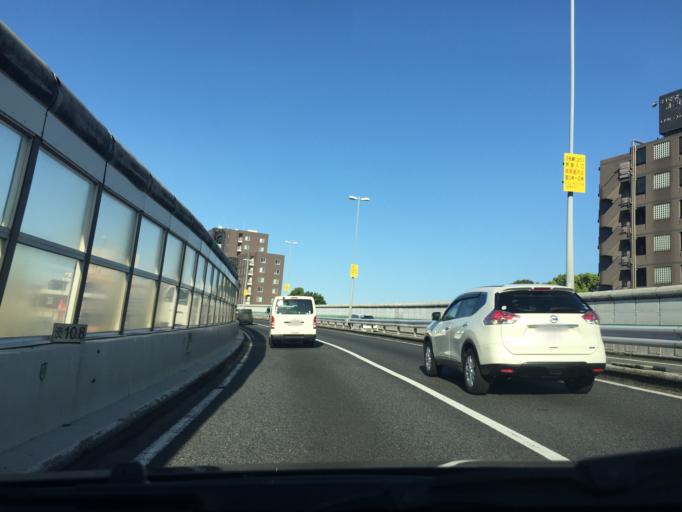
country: JP
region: Tokyo
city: Tokyo
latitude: 35.6242
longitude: 139.6371
